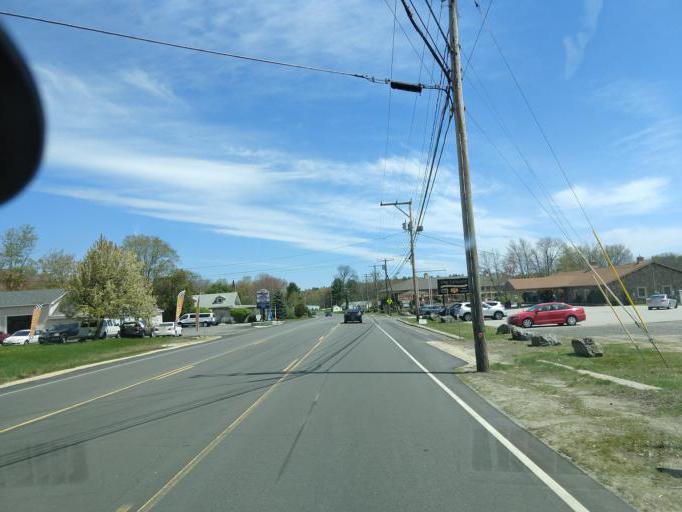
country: US
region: New Hampshire
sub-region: Rockingham County
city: Seabrook
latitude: 42.9033
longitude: -70.8675
